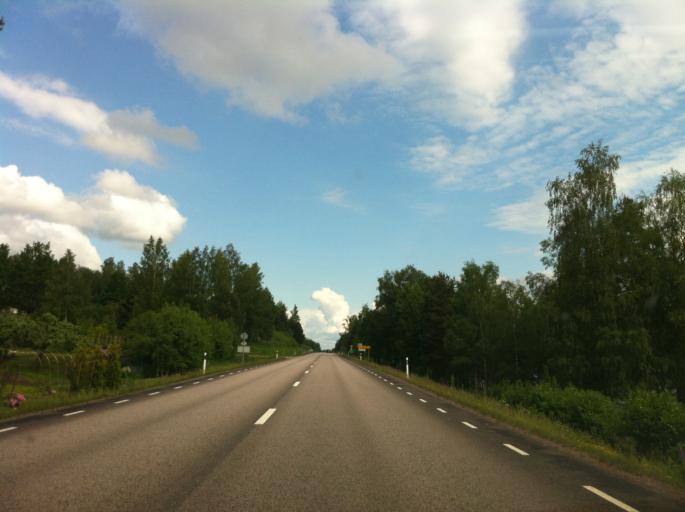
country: SE
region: Vaermland
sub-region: Sunne Kommun
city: Sunne
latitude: 59.8814
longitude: 13.1408
